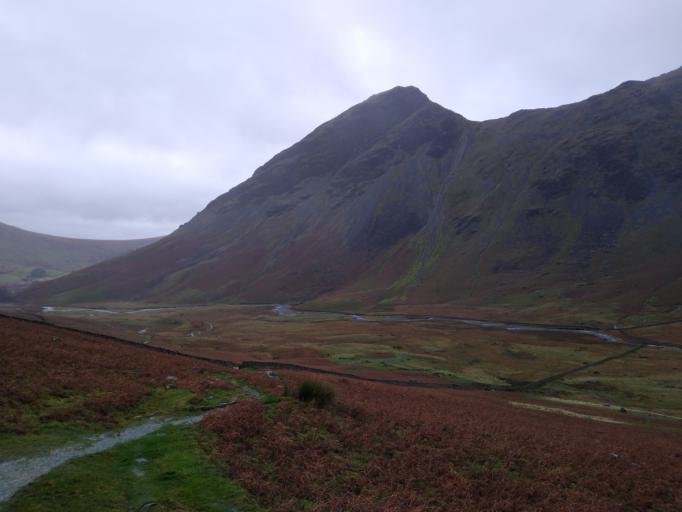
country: GB
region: England
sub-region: Cumbria
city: Keswick
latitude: 54.4835
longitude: -3.2633
